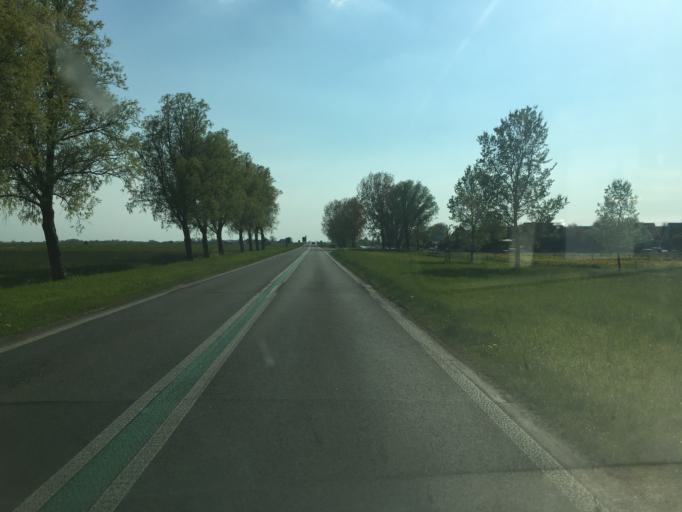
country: NL
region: Friesland
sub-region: Sudwest Fryslan
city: Workum
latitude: 52.9740
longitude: 5.4504
